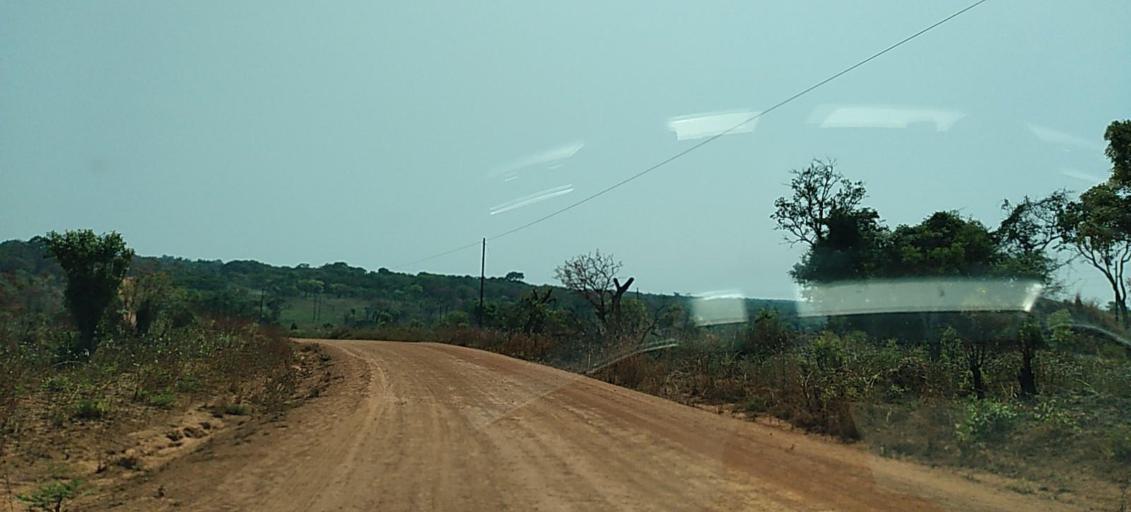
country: ZM
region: North-Western
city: Kansanshi
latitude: -11.9973
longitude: 26.6140
